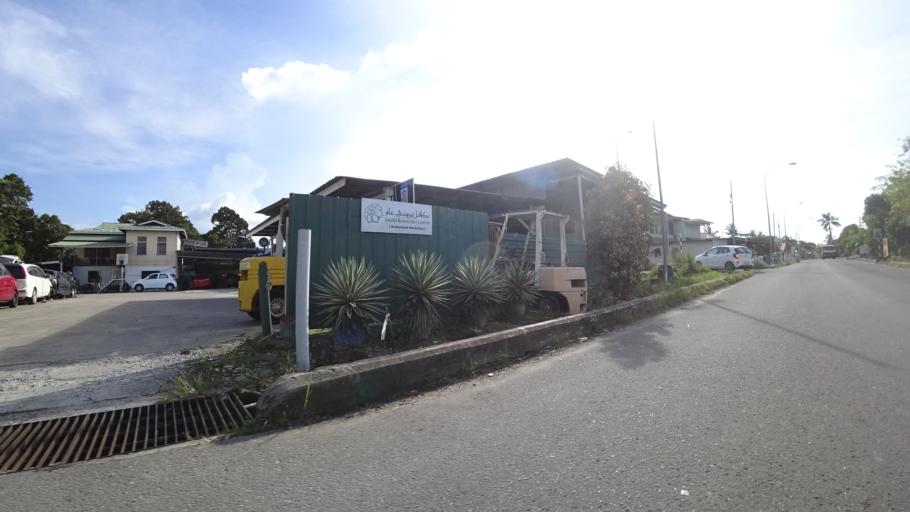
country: BN
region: Brunei and Muara
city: Bandar Seri Begawan
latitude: 4.8470
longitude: 114.8739
